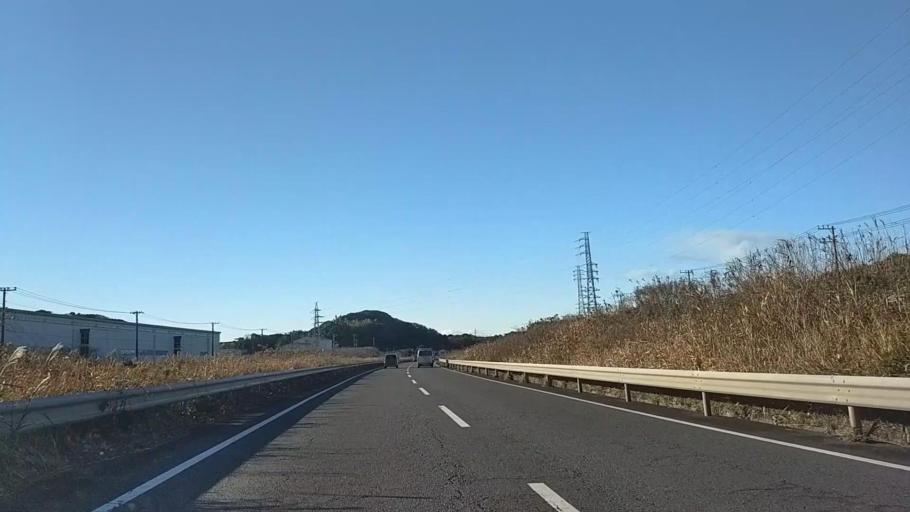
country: JP
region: Chiba
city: Kisarazu
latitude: 35.3599
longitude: 139.9105
